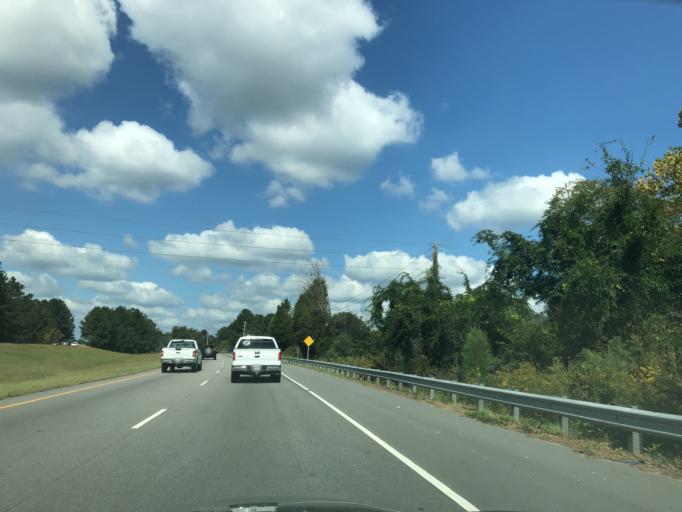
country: US
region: North Carolina
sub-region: Wake County
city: Wake Forest
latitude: 35.9231
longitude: -78.5433
